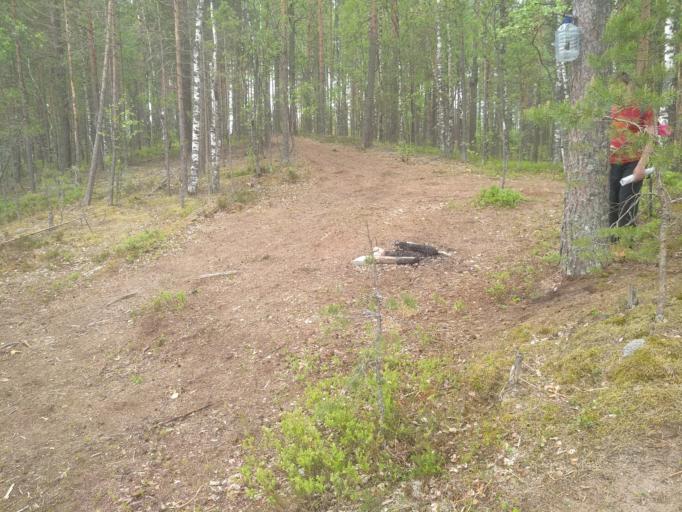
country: RU
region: Leningrad
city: Michurinskoye
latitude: 60.5970
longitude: 29.9201
